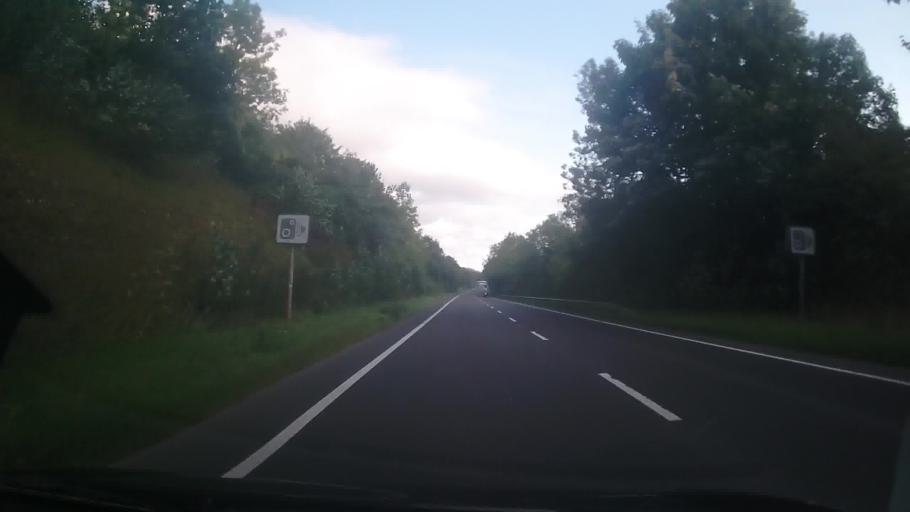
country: GB
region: England
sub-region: Shropshire
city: Craven Arms
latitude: 52.4191
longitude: -2.8199
